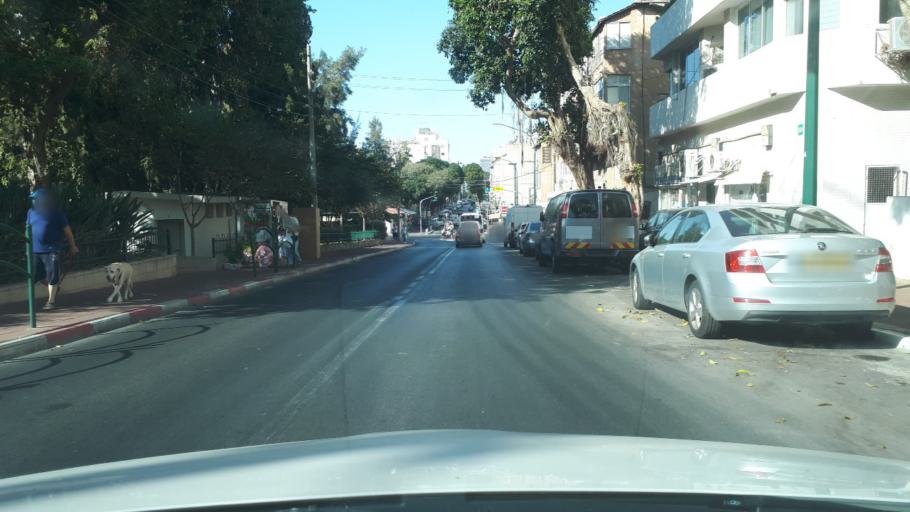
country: IL
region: Tel Aviv
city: Giv`atayim
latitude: 32.0737
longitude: 34.8230
